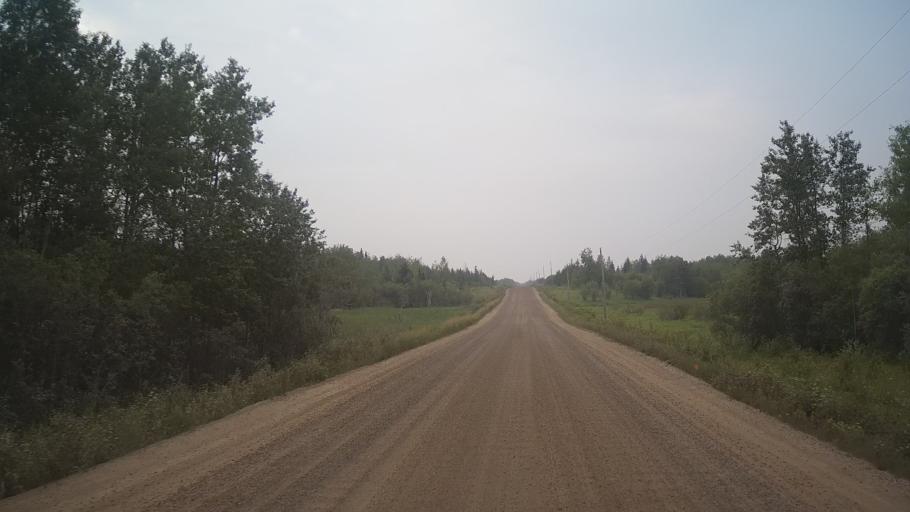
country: CA
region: Ontario
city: Hearst
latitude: 49.6335
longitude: -83.2783
